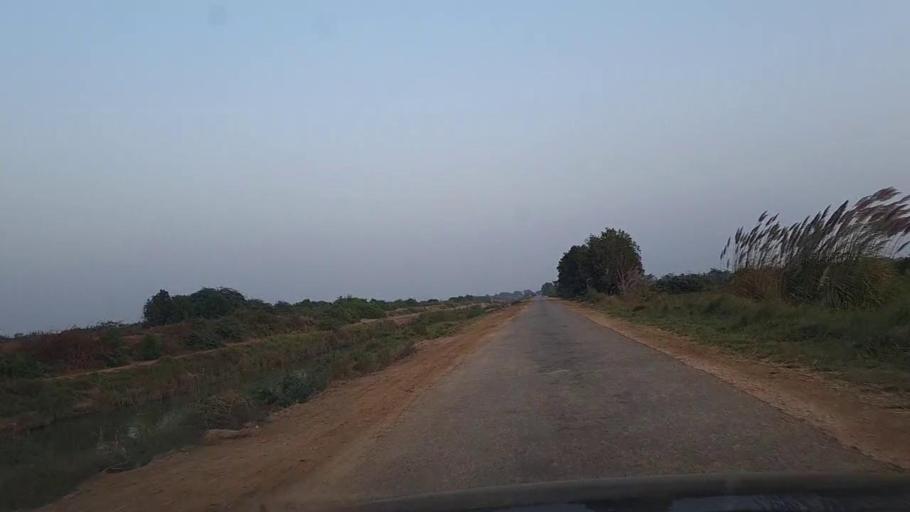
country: PK
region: Sindh
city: Mirpur Sakro
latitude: 24.6305
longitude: 67.6352
